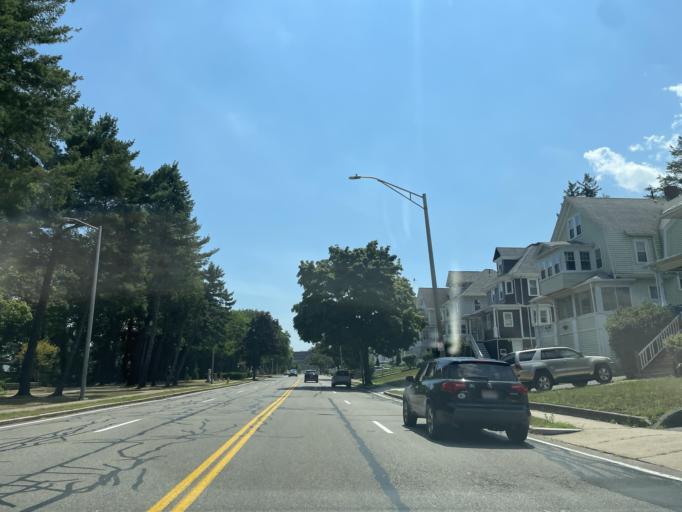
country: US
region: Massachusetts
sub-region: Norfolk County
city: Quincy
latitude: 42.2549
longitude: -71.0088
